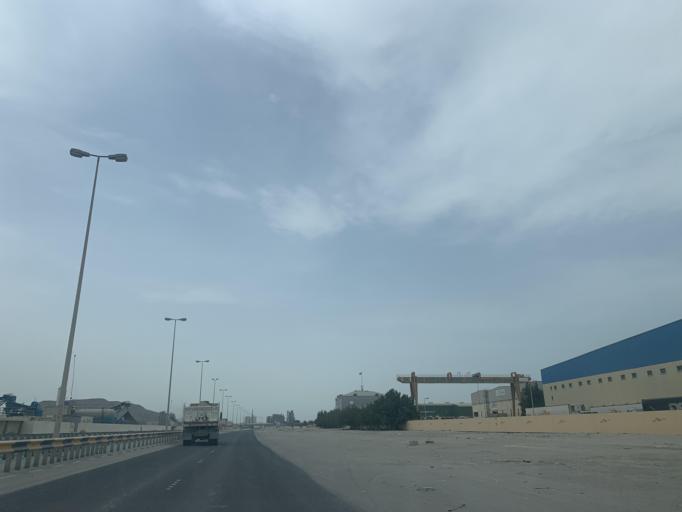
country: BH
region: Muharraq
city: Al Hadd
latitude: 26.2039
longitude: 50.6603
